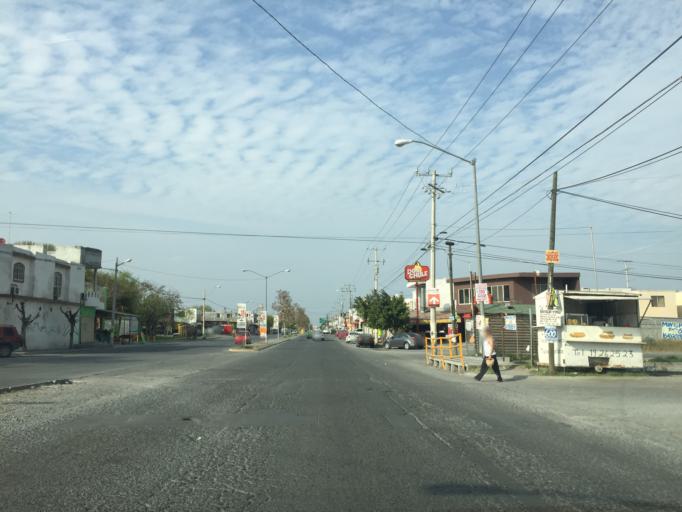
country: MX
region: Nuevo Leon
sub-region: Apodaca
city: Fraccionamiento Cosmopolis Octavo Sector
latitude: 25.7934
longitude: -100.2487
